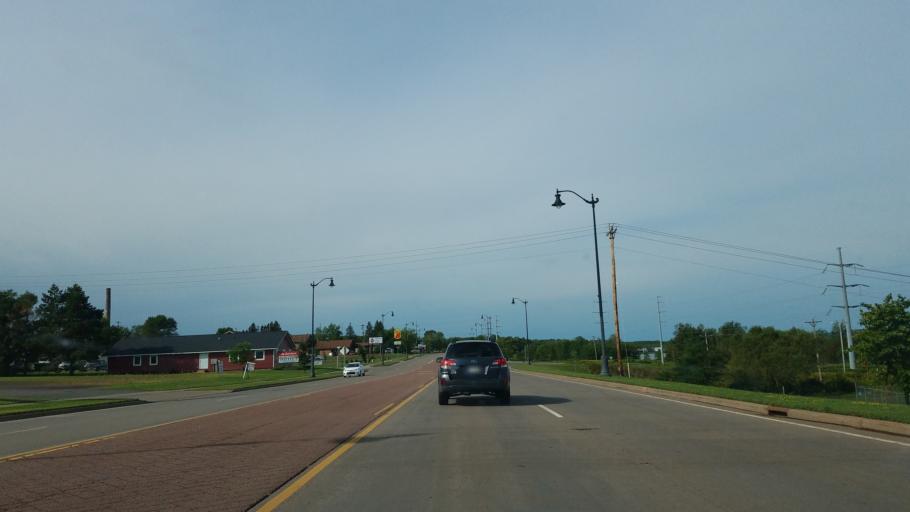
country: US
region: Wisconsin
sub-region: Ashland County
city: Ashland
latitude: 46.5855
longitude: -90.9000
